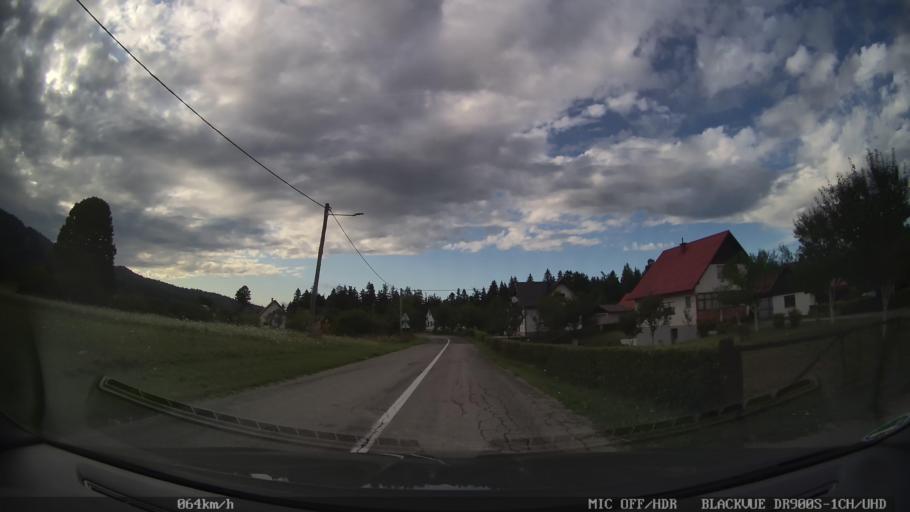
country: HR
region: Licko-Senjska
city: Jezerce
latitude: 44.9468
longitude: 15.5390
